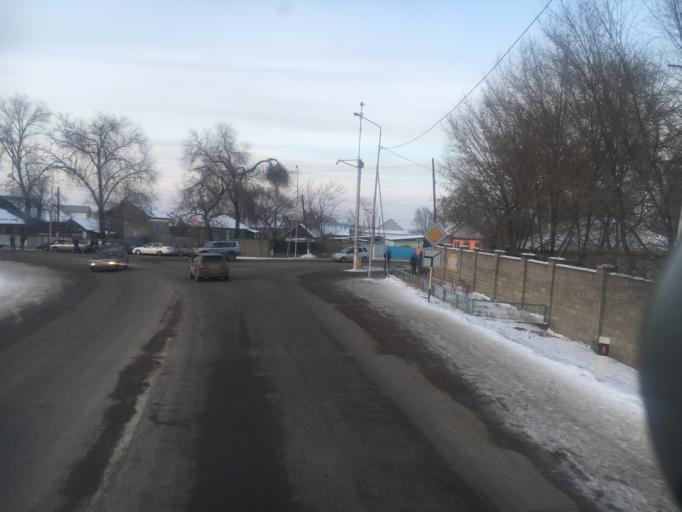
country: KZ
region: Almaty Oblysy
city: Burunday
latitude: 43.3768
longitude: 76.6419
